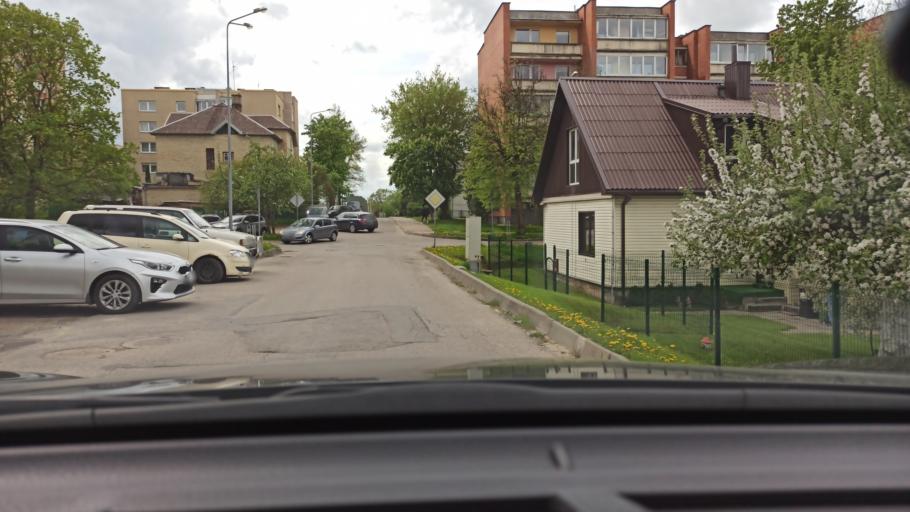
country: LT
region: Siauliu apskritis
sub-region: Siauliai
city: Siauliai
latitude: 55.9350
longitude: 23.3031
